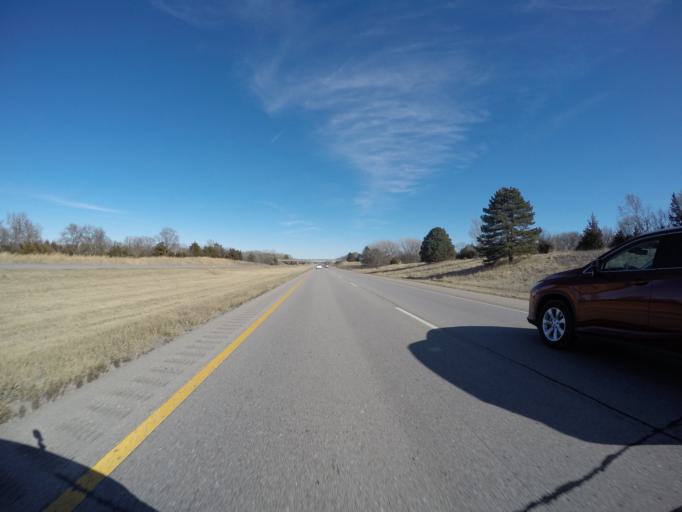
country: US
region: Nebraska
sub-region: Seward County
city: Milford
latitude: 40.8203
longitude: -96.8966
